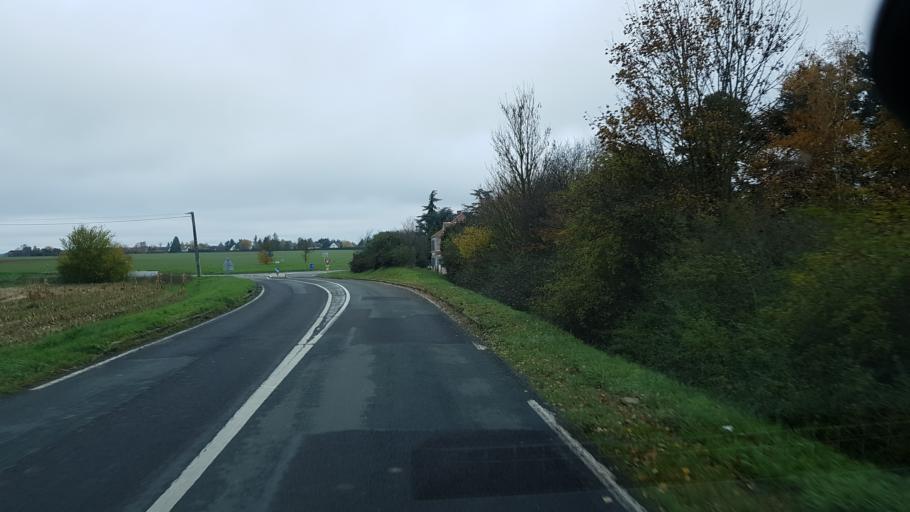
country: FR
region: Ile-de-France
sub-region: Departement des Yvelines
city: Dampierre-en-Yvelines
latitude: 48.7188
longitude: 2.0024
